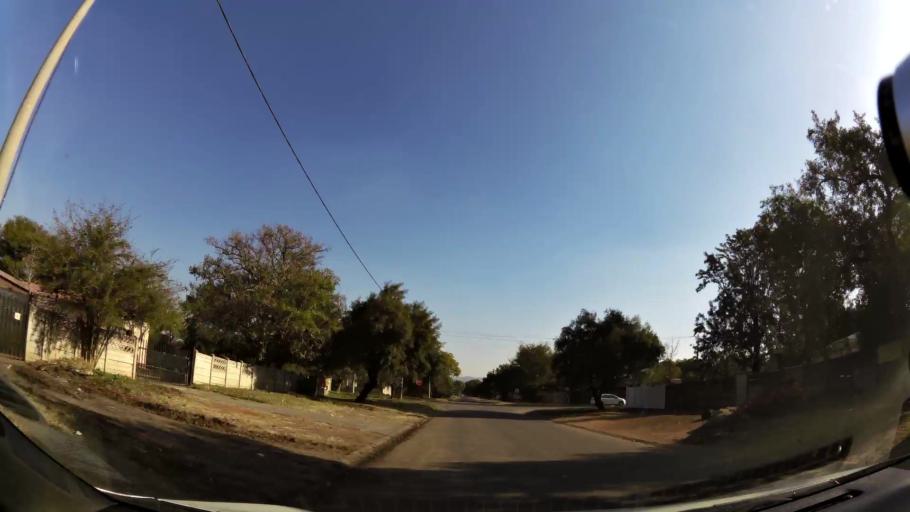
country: ZA
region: North-West
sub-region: Bojanala Platinum District Municipality
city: Rustenburg
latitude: -25.6586
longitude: 27.2628
